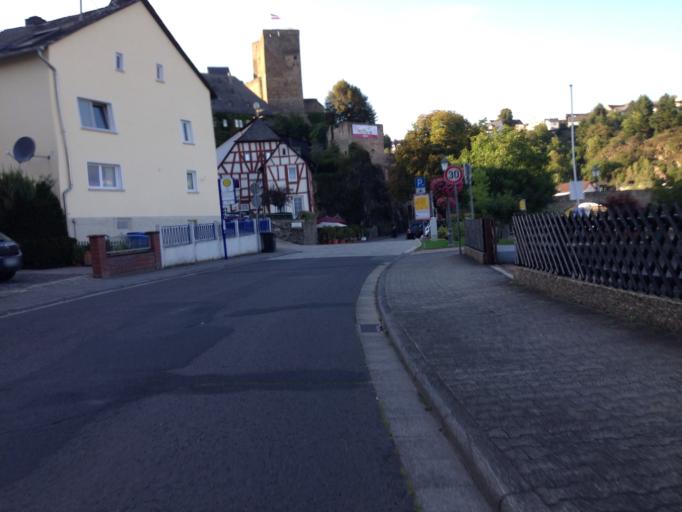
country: DE
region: Hesse
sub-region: Regierungsbezirk Giessen
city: Runkel
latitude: 50.4044
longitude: 8.1576
